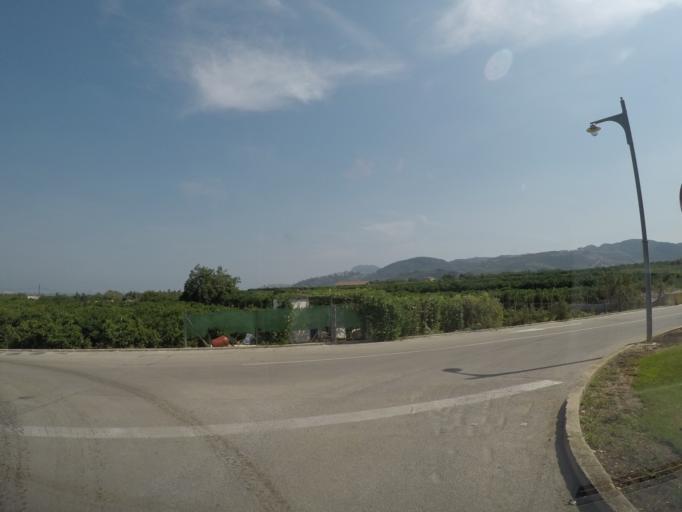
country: ES
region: Valencia
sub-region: Provincia de Alicante
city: Pego
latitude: 38.8453
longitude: -0.0956
